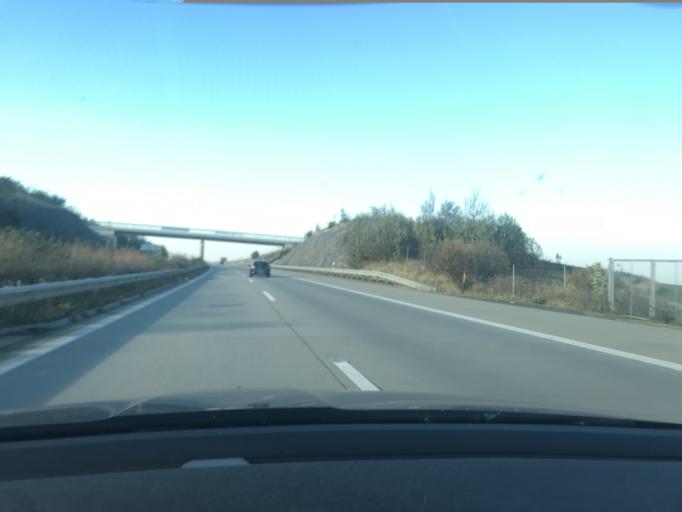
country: DE
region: Saxony
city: Liebstadt
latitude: 50.8498
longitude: 13.8802
